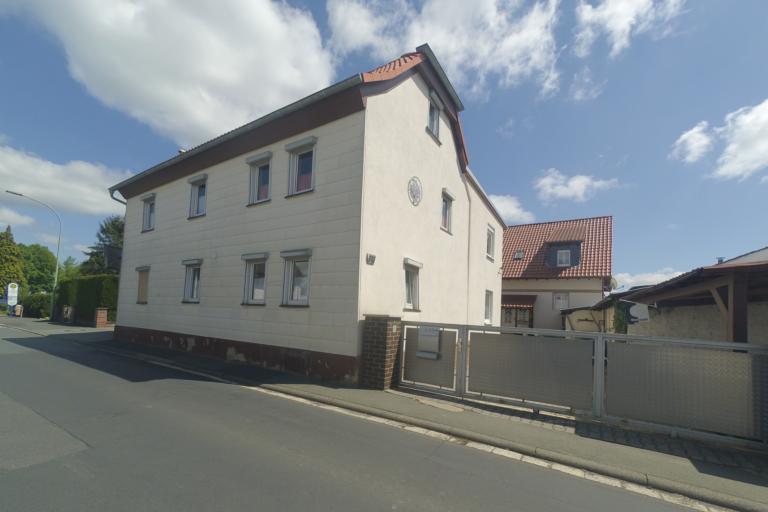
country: DE
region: Hesse
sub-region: Regierungsbezirk Darmstadt
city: Karben
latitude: 50.2446
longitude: 8.7146
